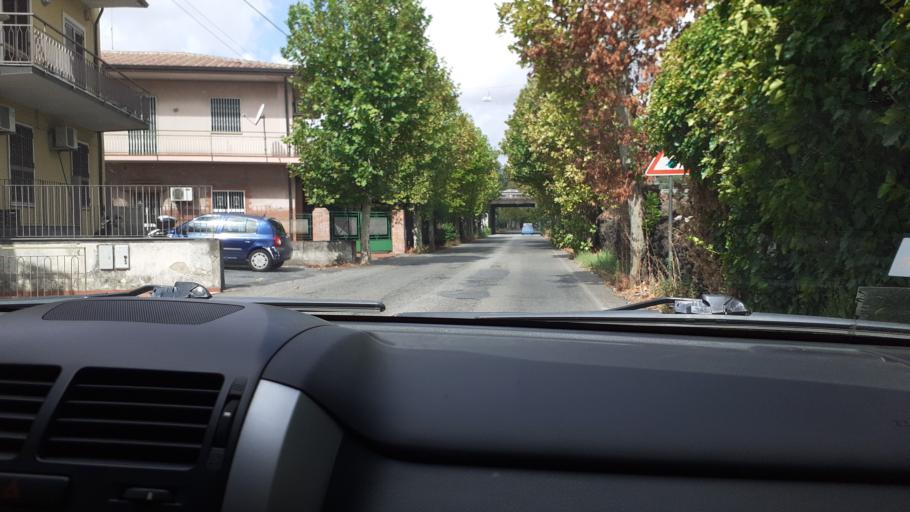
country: IT
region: Sicily
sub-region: Catania
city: San Gregorio di Catania
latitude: 37.5680
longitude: 15.1059
